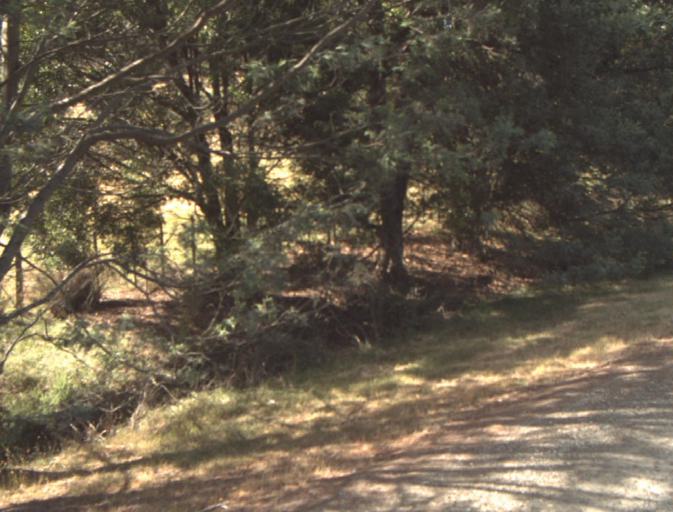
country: AU
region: Tasmania
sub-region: Launceston
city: Mayfield
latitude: -41.2890
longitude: 147.2174
